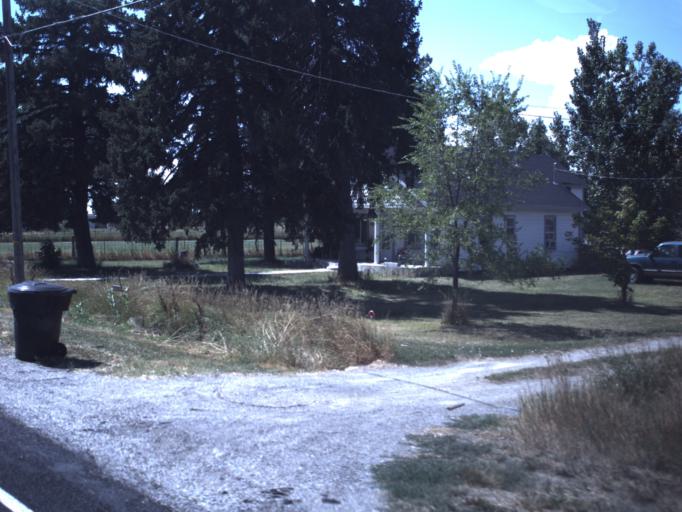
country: US
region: Utah
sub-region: Box Elder County
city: Honeyville
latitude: 41.6071
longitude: -112.1273
